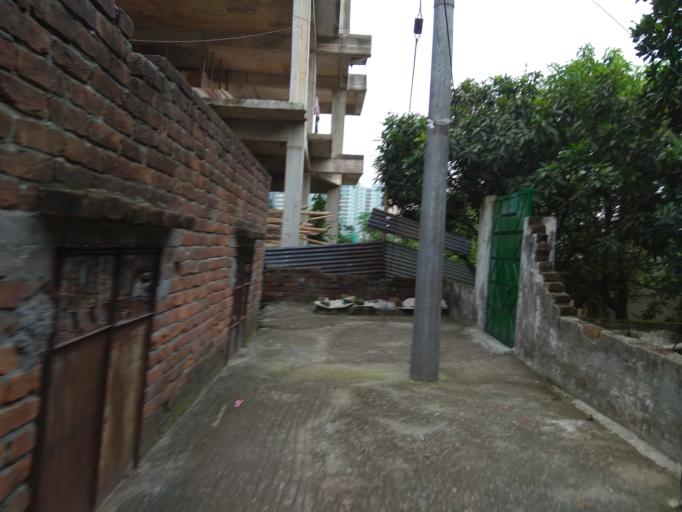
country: BD
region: Dhaka
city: Tungi
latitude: 23.8131
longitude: 90.3825
